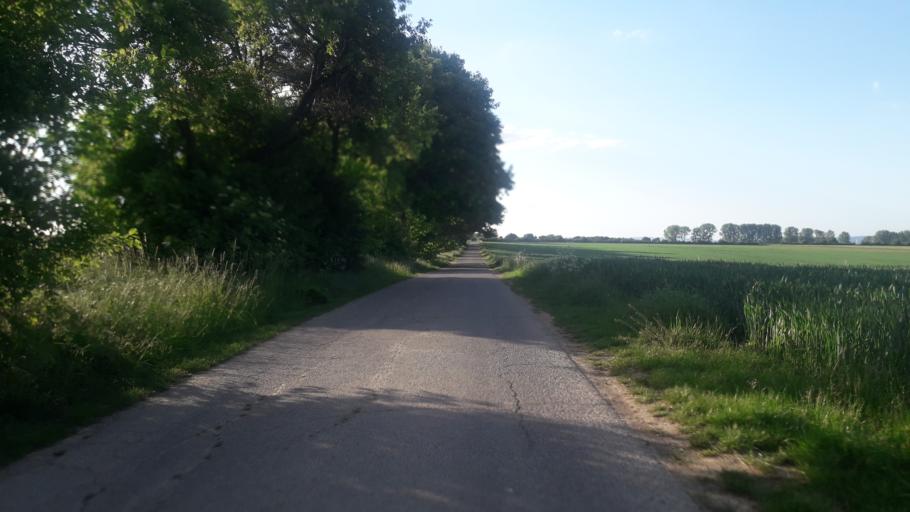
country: DE
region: North Rhine-Westphalia
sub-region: Regierungsbezirk Detmold
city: Paderborn
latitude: 51.6804
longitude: 8.7703
